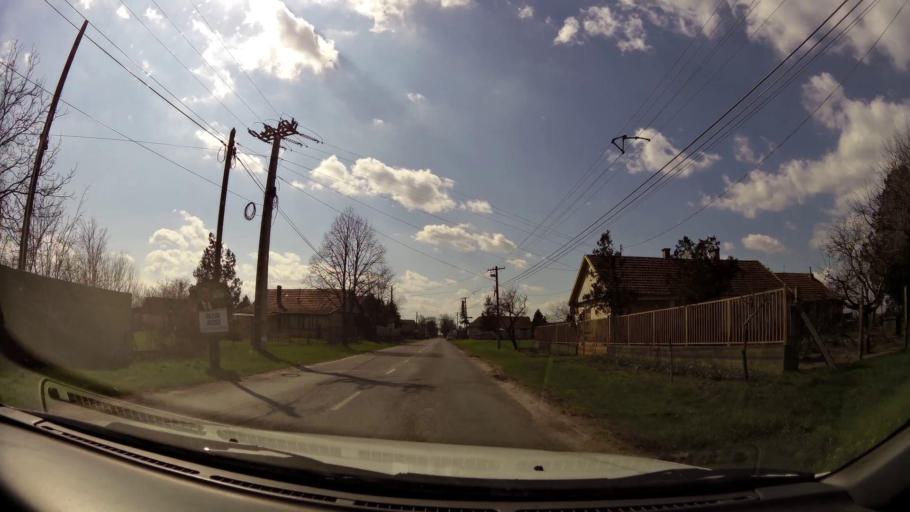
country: HU
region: Pest
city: Tapiogyorgye
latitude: 47.3397
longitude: 19.9380
